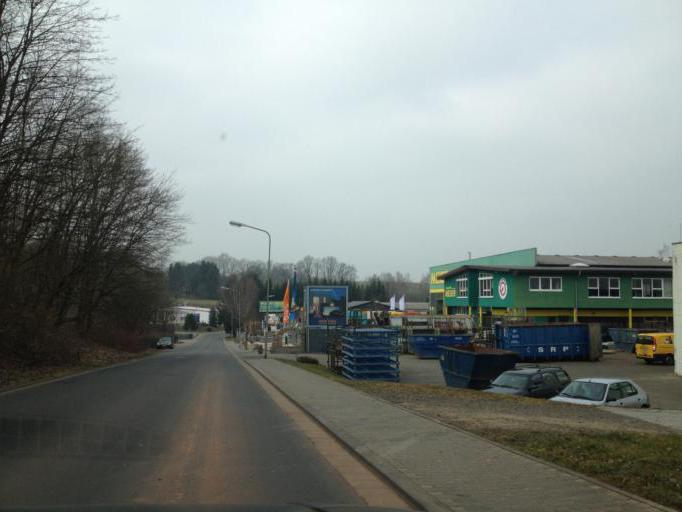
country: DE
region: Saarland
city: Sankt Wendel
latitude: 49.4645
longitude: 7.1418
